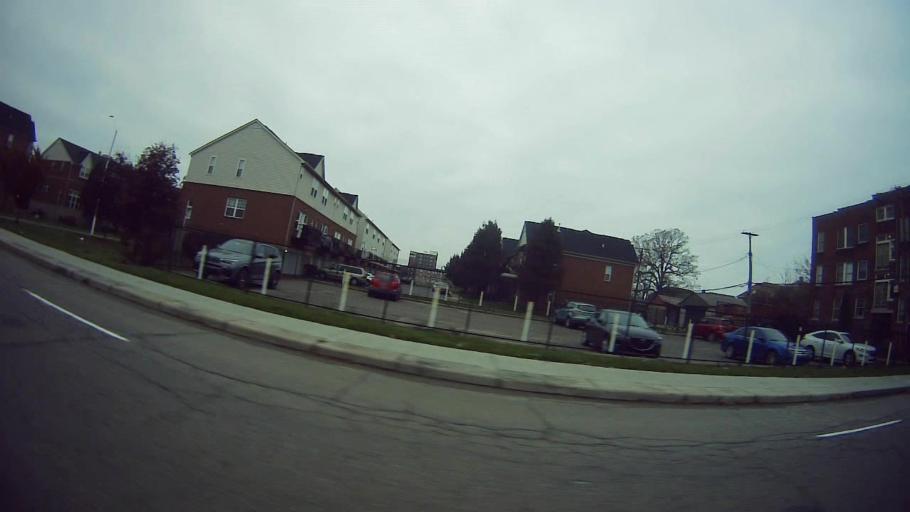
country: US
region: Michigan
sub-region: Wayne County
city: Hamtramck
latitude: 42.3643
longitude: -83.0635
